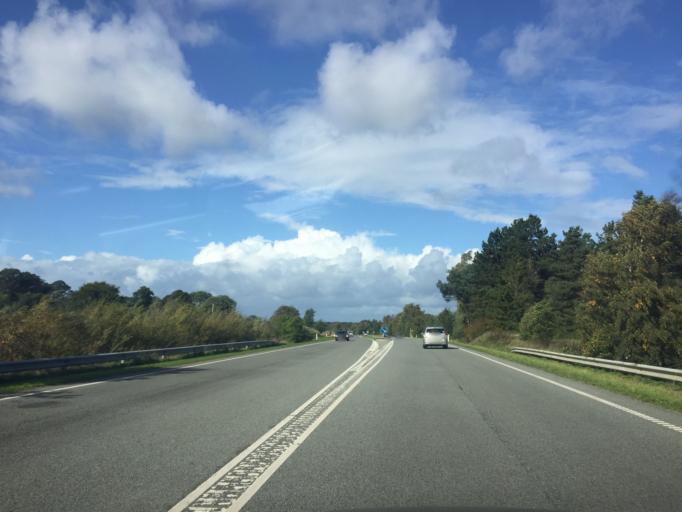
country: DK
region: Capital Region
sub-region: Gribskov Kommune
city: Helsinge
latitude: 56.0297
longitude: 12.1674
